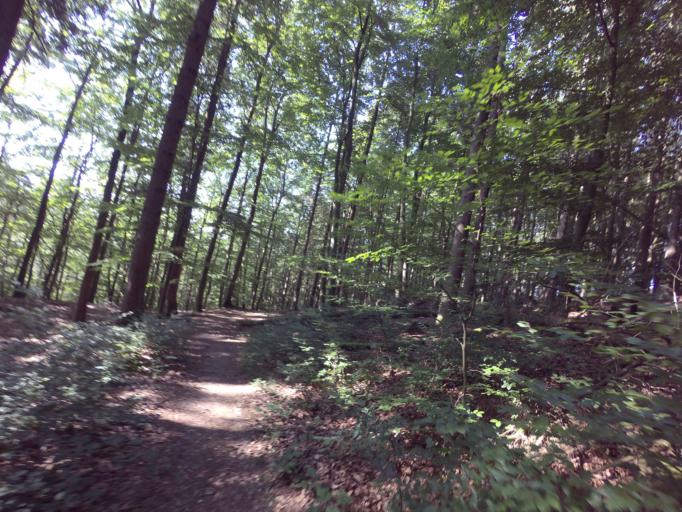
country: DE
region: North Rhine-Westphalia
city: Heimbach
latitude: 50.6109
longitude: 6.4253
